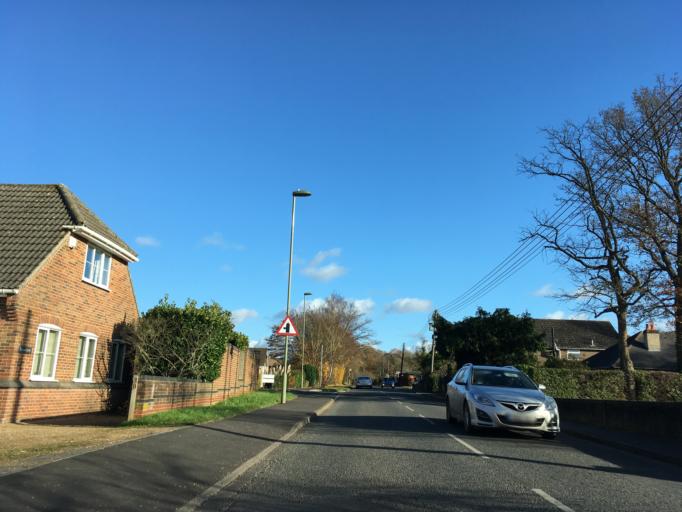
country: GB
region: England
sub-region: Hampshire
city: Colden Common
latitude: 50.9917
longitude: -1.3137
